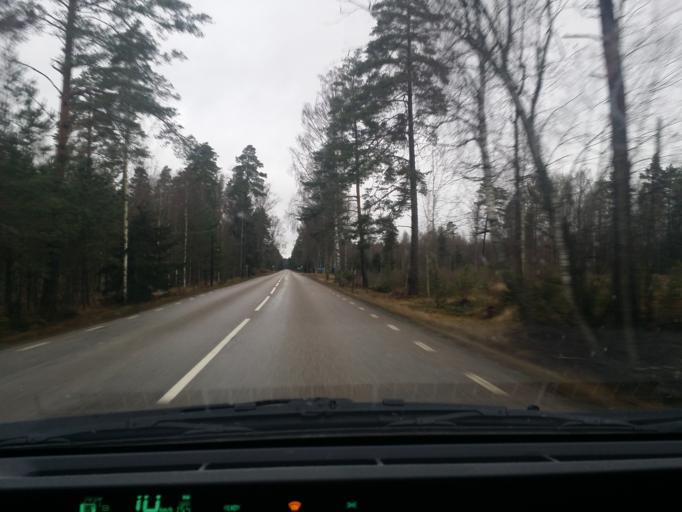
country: SE
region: Vaestmanland
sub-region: Sala Kommun
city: Sala
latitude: 59.8251
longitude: 16.5244
